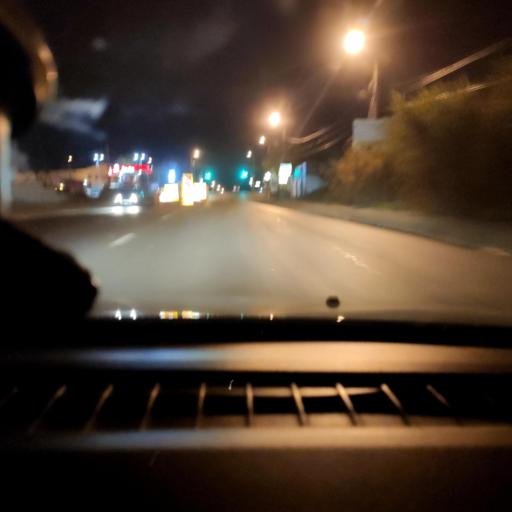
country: RU
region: Samara
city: Samara
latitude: 53.1843
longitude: 50.1617
